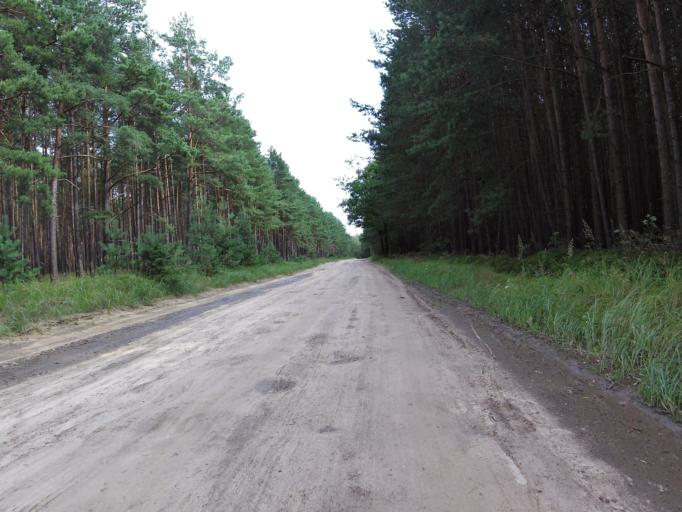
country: DE
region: Brandenburg
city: Lychen
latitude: 53.2385
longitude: 13.2325
